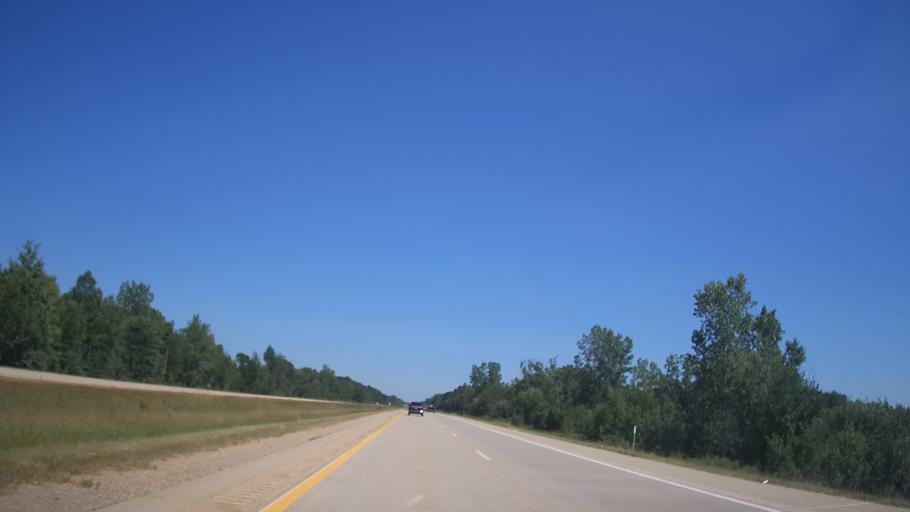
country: US
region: Michigan
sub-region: Midland County
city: Coleman
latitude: 43.7435
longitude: -84.5265
